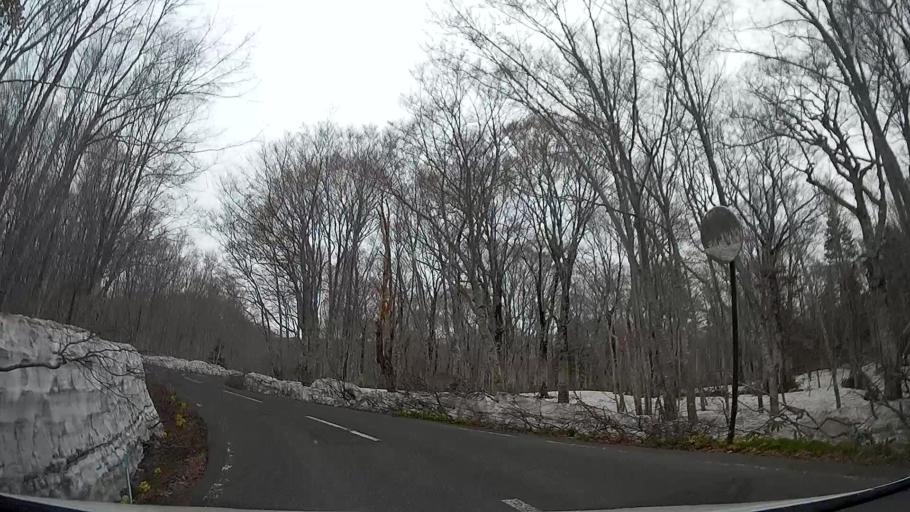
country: JP
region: Aomori
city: Aomori Shi
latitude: 40.6308
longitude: 140.9242
